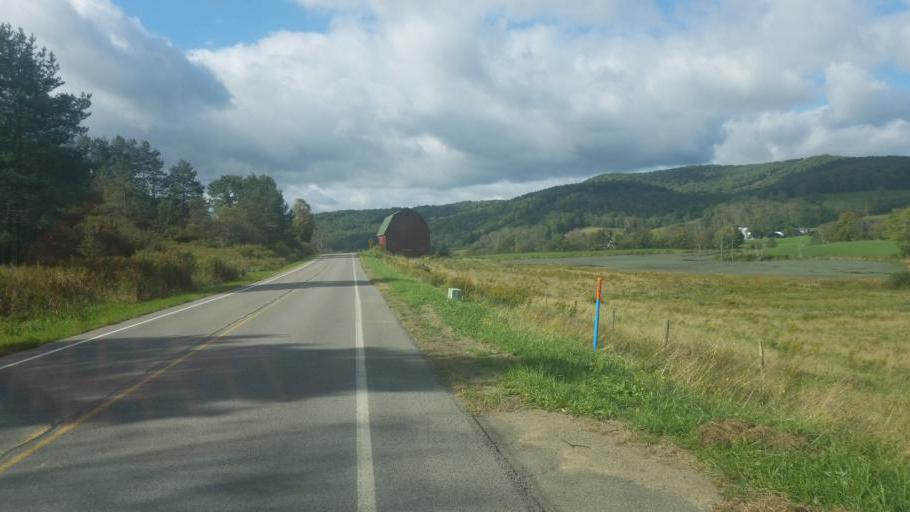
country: US
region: New York
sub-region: Cattaraugus County
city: Weston Mills
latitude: 42.1360
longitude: -78.3344
